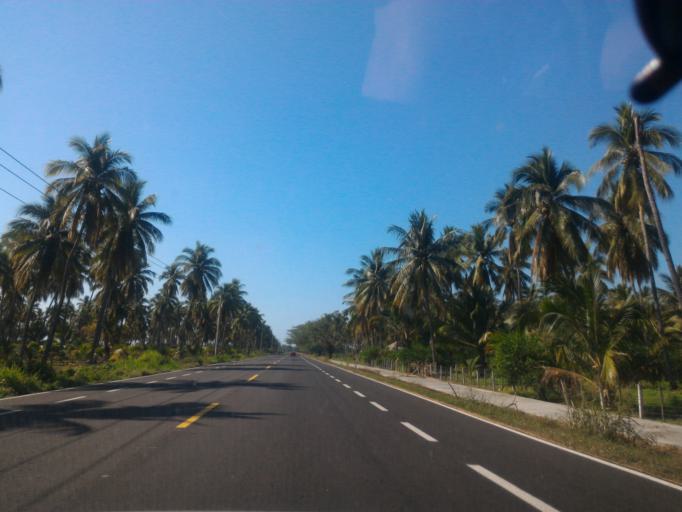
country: MX
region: Colima
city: Tecoman
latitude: 18.8849
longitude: -103.9229
